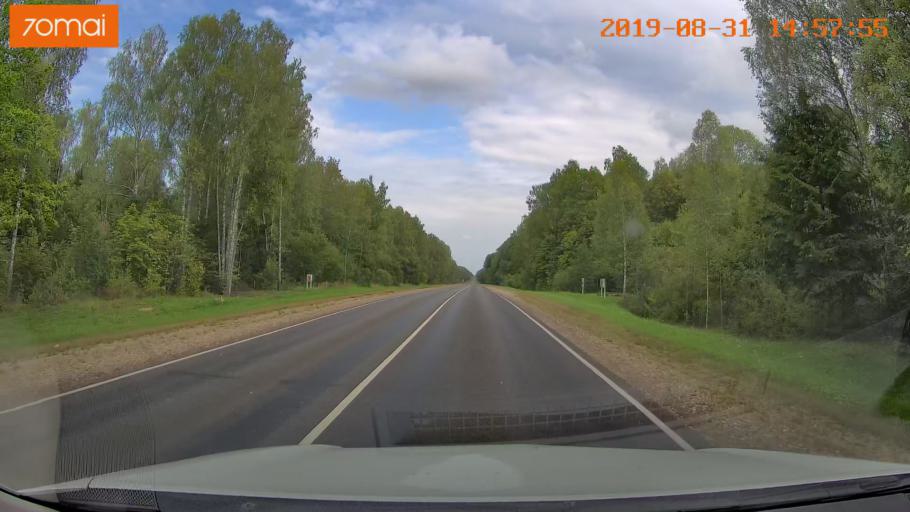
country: RU
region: Kaluga
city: Spas-Demensk
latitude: 54.3138
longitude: 33.9689
